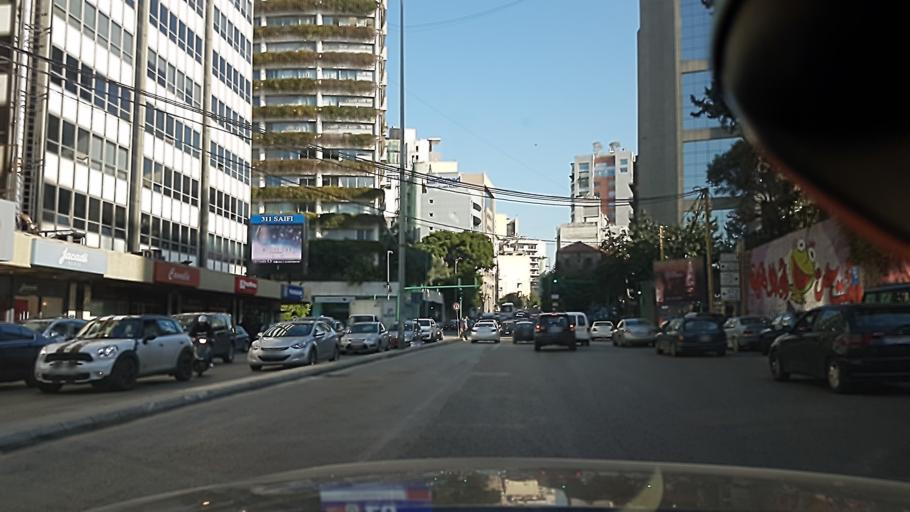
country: LB
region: Beyrouth
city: Beirut
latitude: 33.8924
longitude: 35.5104
